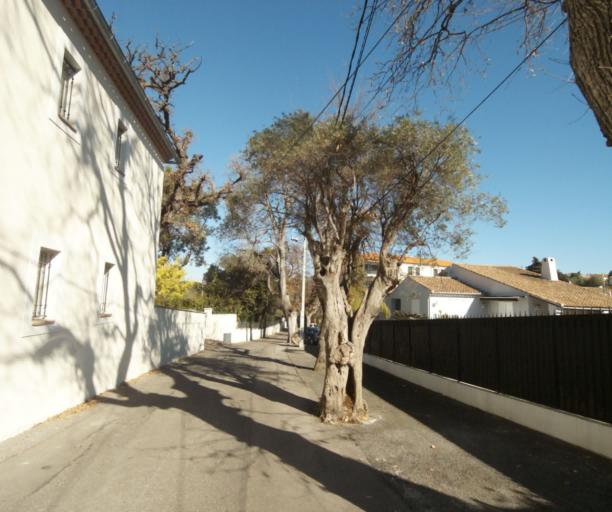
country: FR
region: Provence-Alpes-Cote d'Azur
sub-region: Departement des Alpes-Maritimes
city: Antibes
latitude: 43.5654
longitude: 7.1202
